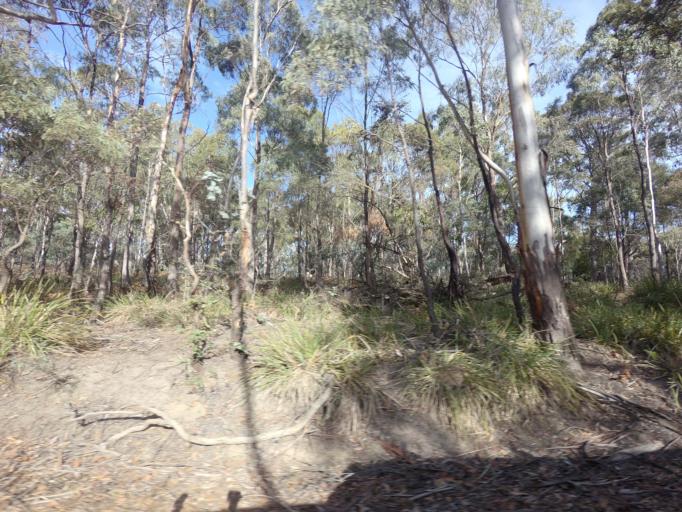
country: AU
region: Tasmania
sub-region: Sorell
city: Sorell
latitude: -42.5244
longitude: 147.4699
